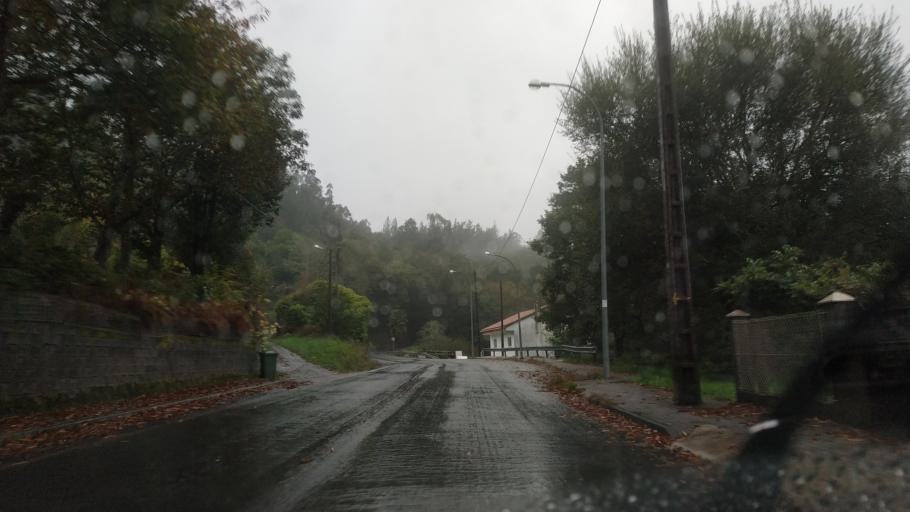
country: ES
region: Galicia
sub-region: Provincia da Coruna
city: Negreira
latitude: 42.9065
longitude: -8.7442
